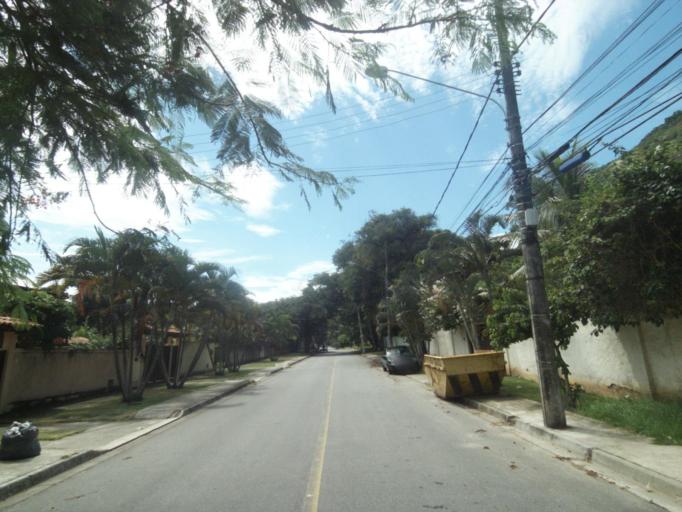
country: BR
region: Rio de Janeiro
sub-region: Niteroi
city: Niteroi
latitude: -22.9561
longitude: -43.0253
